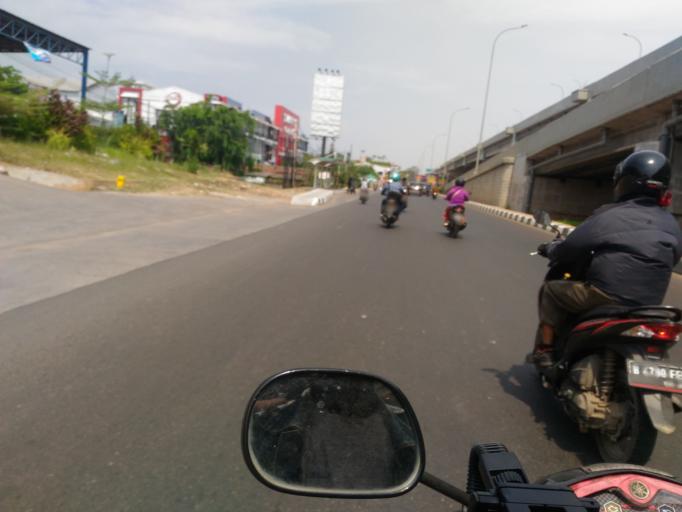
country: ID
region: West Java
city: Bekasi
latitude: -6.2483
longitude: 106.9303
